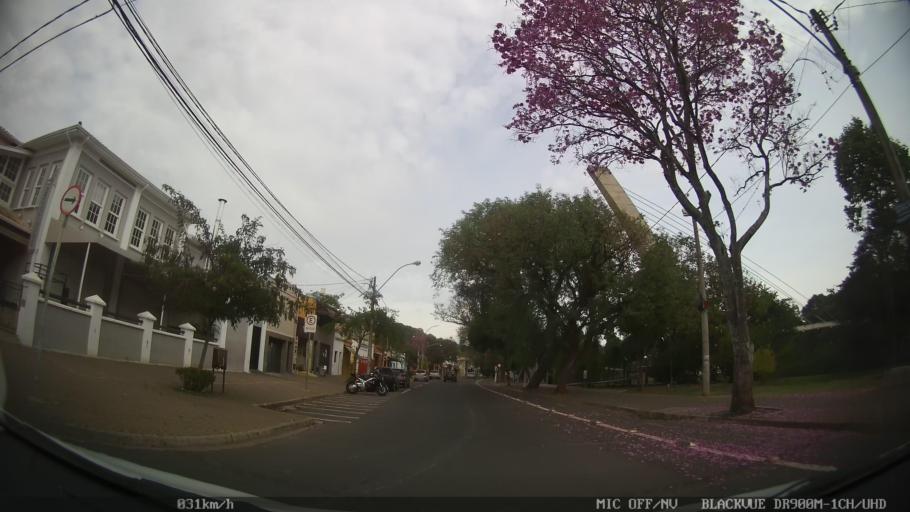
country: BR
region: Sao Paulo
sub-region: Piracicaba
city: Piracicaba
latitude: -22.7232
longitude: -47.6563
